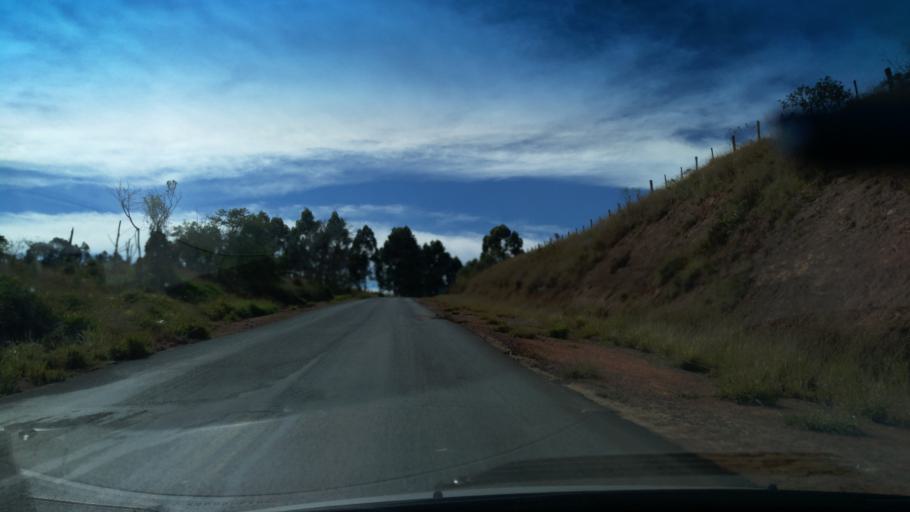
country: BR
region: Minas Gerais
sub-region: Andradas
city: Andradas
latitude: -22.0439
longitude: -46.3396
